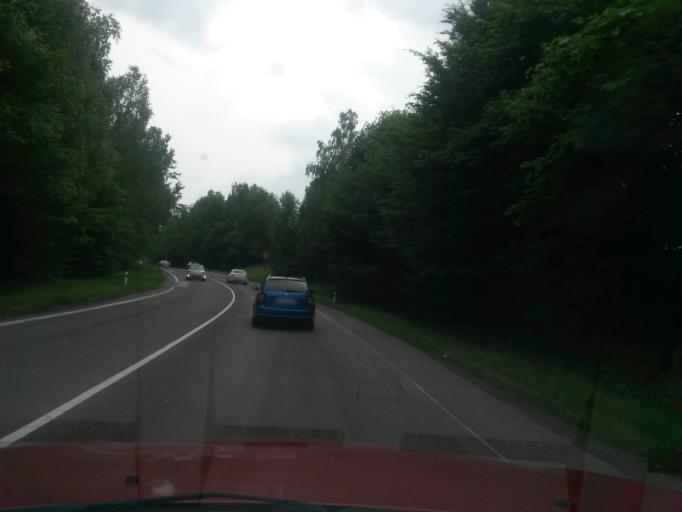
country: SK
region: Presovsky
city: Giraltovce
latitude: 49.0508
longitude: 21.4249
